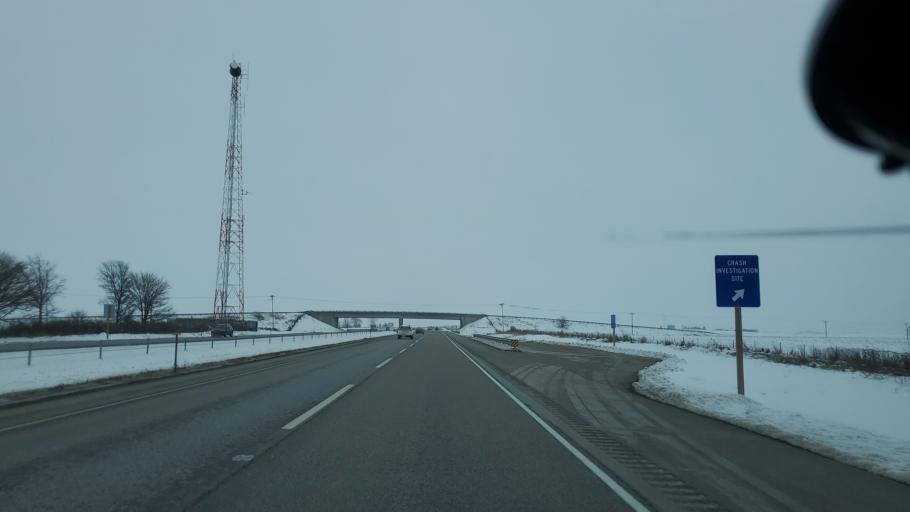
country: US
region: Illinois
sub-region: Ogle County
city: Rochelle
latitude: 41.9035
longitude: -88.9642
